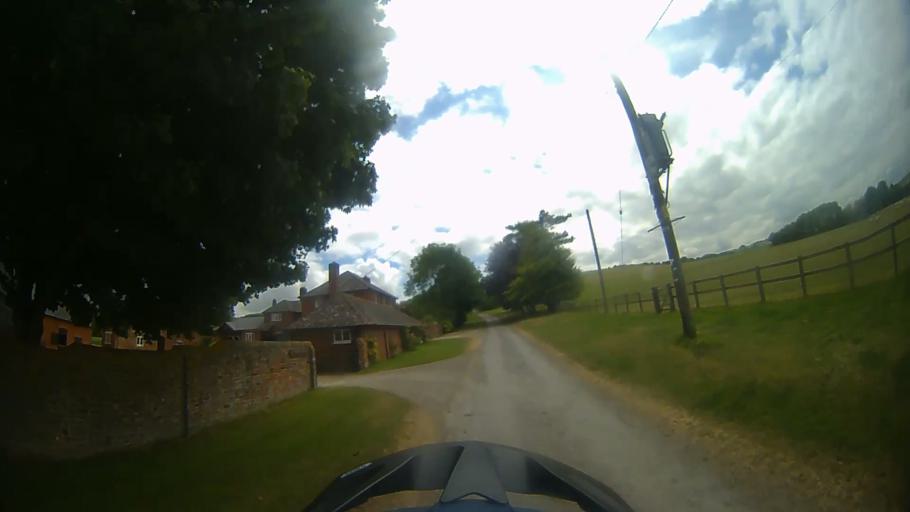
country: GB
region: England
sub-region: Oxfordshire
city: Wantage
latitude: 51.5656
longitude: -1.4466
